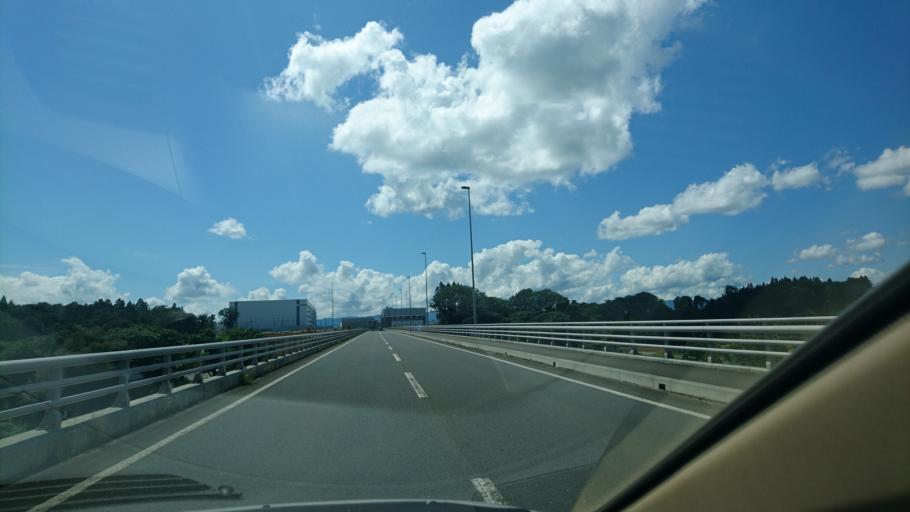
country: JP
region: Iwate
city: Hanamaki
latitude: 39.3398
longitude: 141.1392
